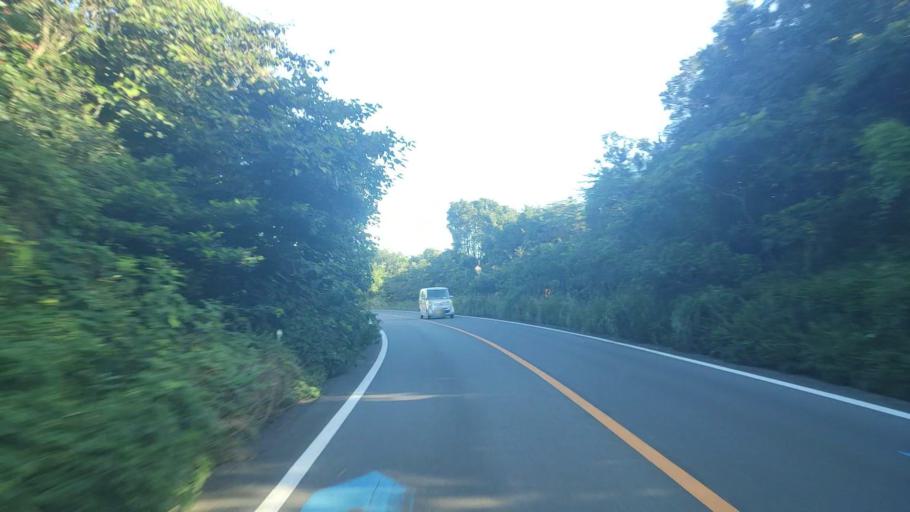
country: JP
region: Mie
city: Toba
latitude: 34.3376
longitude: 136.8395
